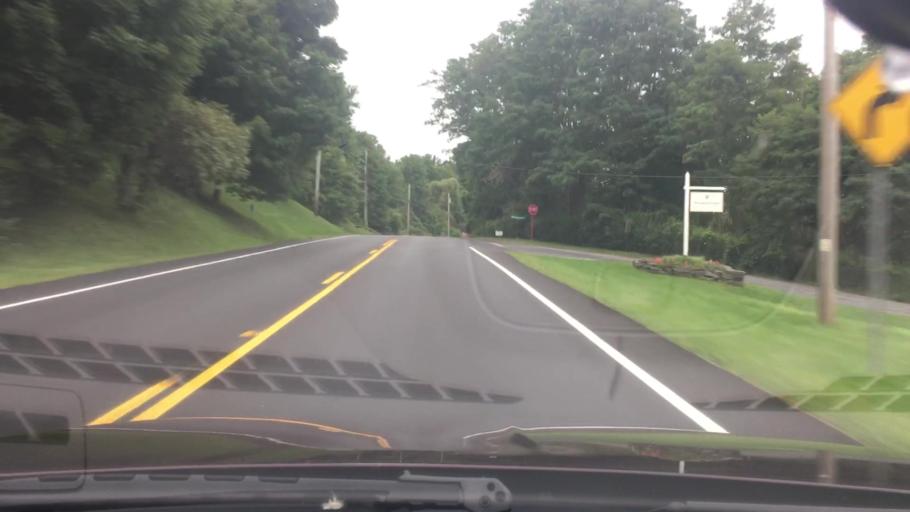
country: US
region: New York
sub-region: Dutchess County
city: Millbrook
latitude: 41.8391
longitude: -73.6099
